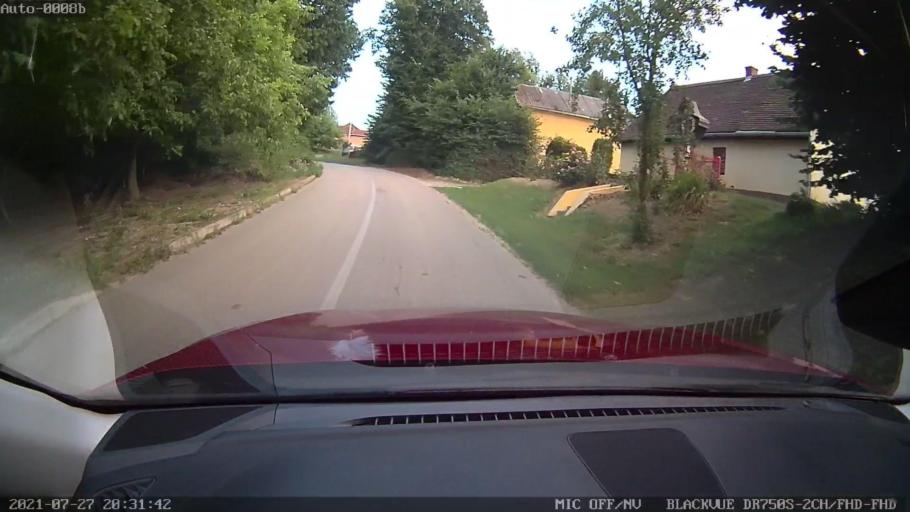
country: HR
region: Varazdinska
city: Jalzabet
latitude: 46.2466
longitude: 16.4726
